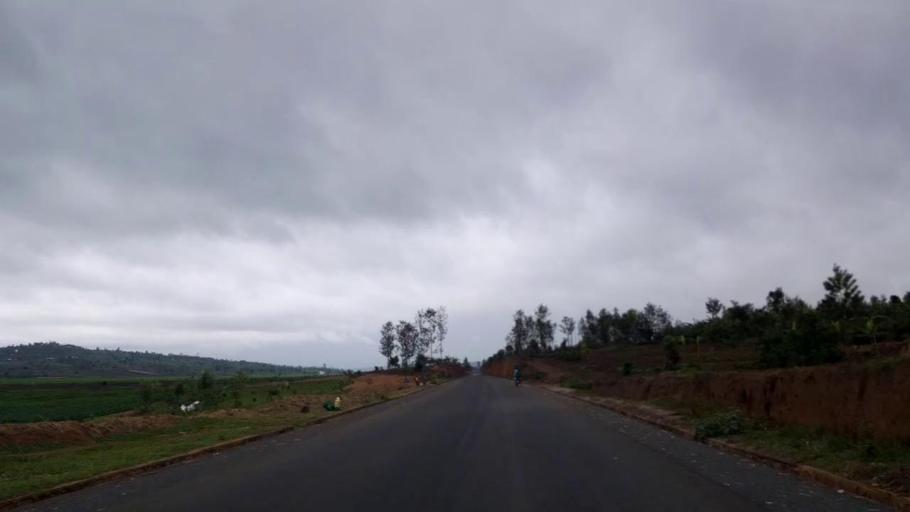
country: RW
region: Northern Province
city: Byumba
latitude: -1.4330
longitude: 30.2613
